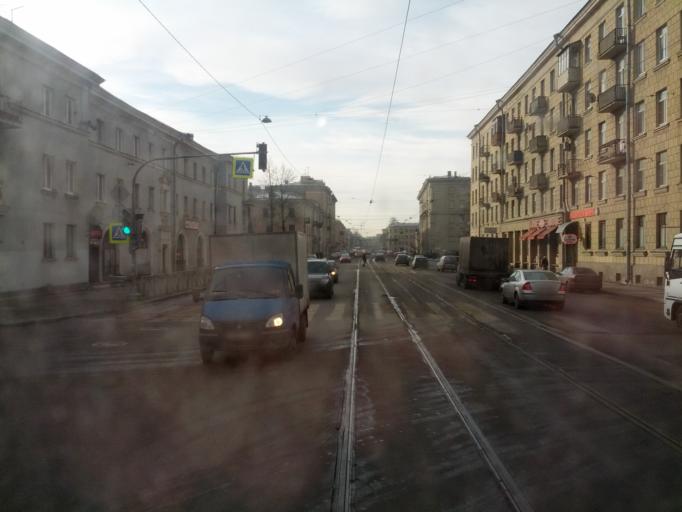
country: RU
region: Leningrad
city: Kalininskiy
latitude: 59.9555
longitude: 30.4153
